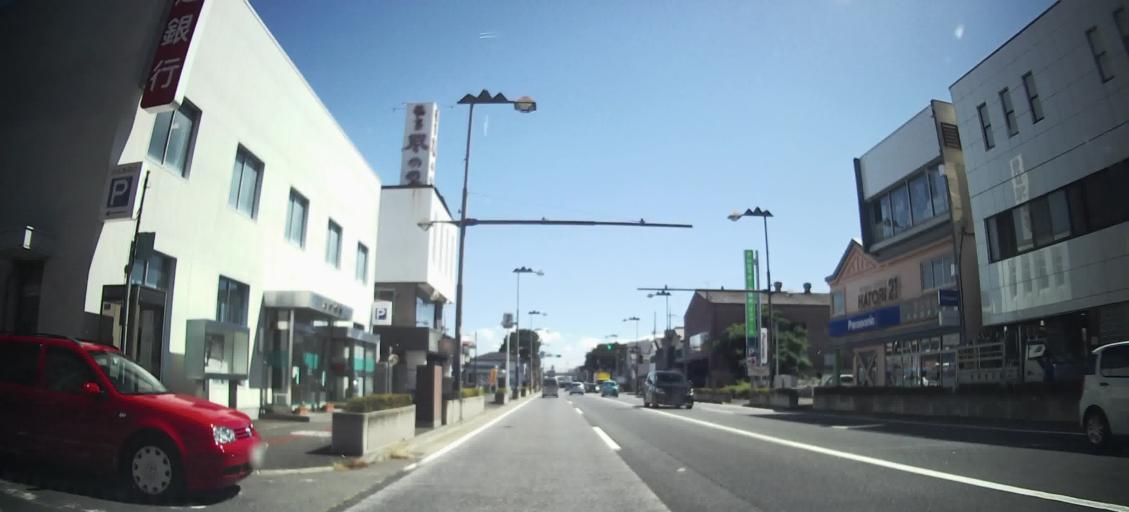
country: JP
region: Gunma
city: Maebashi-shi
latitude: 36.3835
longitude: 139.0901
